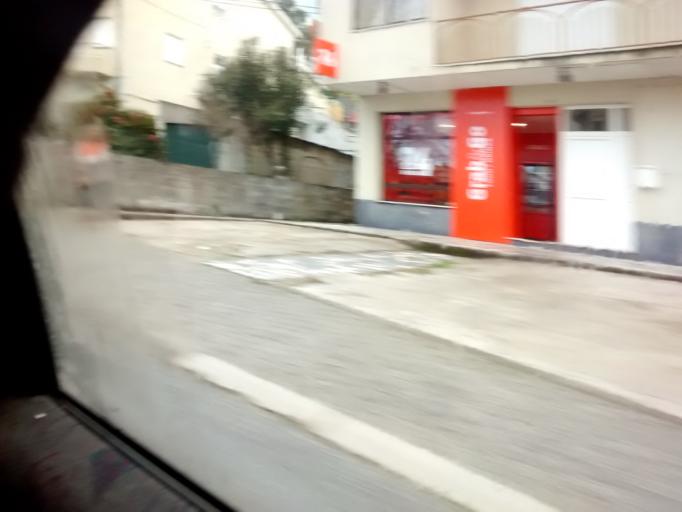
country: PT
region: Guarda
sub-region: Seia
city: Seia
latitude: 40.4131
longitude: -7.7062
